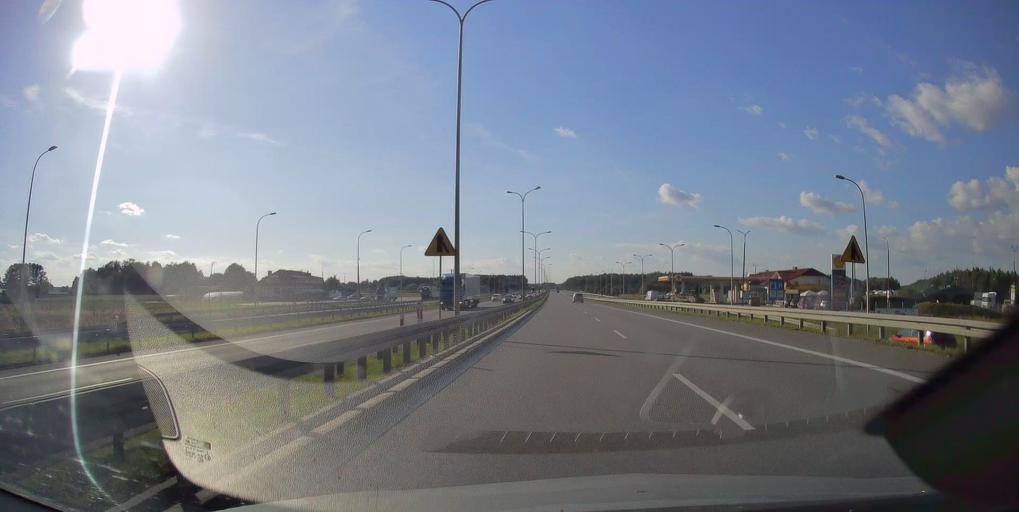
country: PL
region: Masovian Voivodeship
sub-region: Powiat bialobrzeski
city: Stara Blotnica
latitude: 51.5700
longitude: 21.0209
